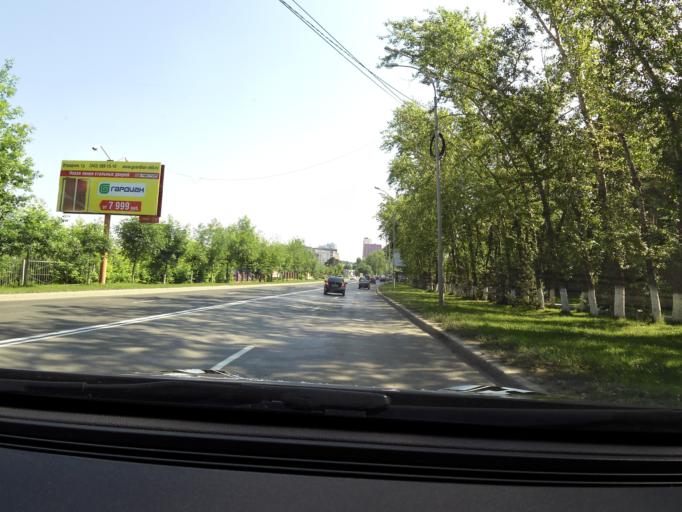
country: RU
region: Sverdlovsk
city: Shirokaya Rechka
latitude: 56.8168
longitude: 60.5297
